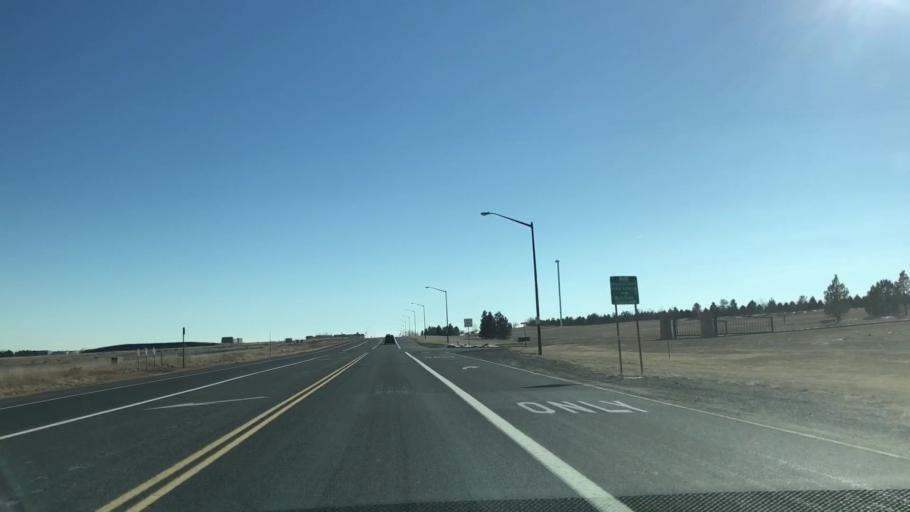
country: US
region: Colorado
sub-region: Weld County
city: Windsor
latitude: 40.4489
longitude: -104.9824
